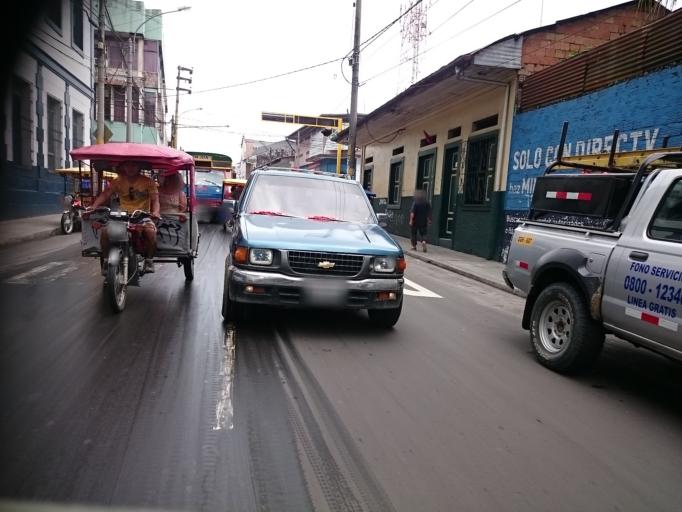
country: PE
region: Loreto
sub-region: Provincia de Maynas
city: Iquitos
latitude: -3.7498
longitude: -73.2466
